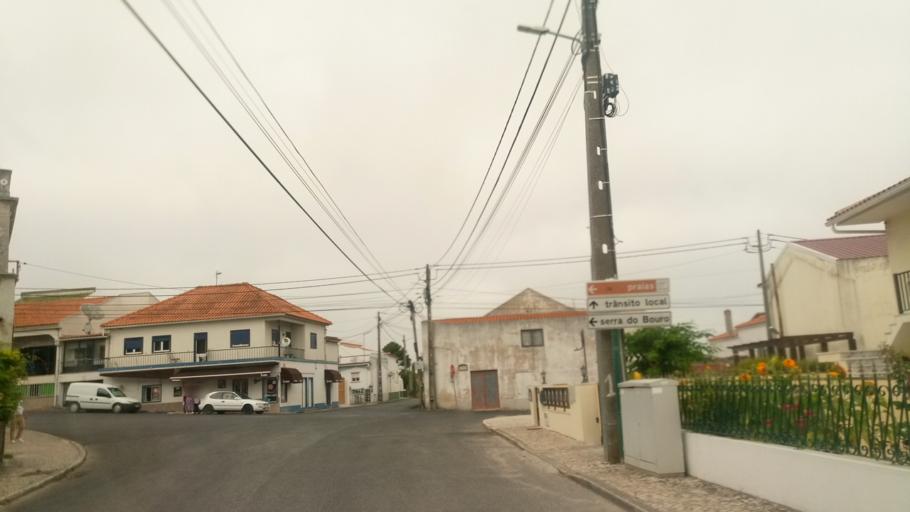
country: PT
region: Leiria
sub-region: Caldas da Rainha
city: Caldas da Rainha
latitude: 39.4367
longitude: -9.1526
